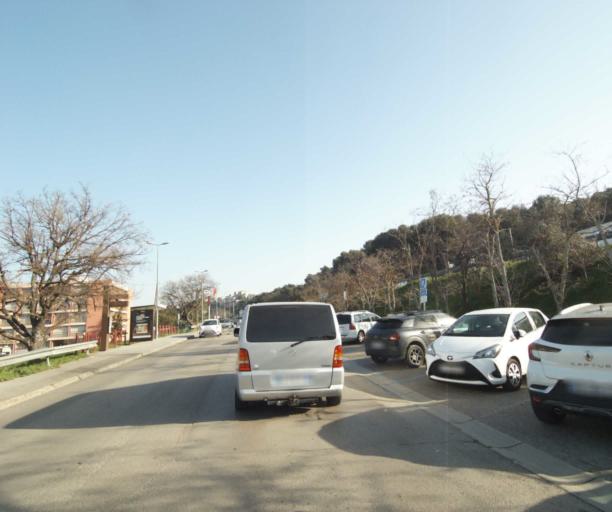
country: FR
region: Provence-Alpes-Cote d'Azur
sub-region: Departement des Bouches-du-Rhone
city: Les Pennes-Mirabeau
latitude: 43.4133
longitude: 5.3014
